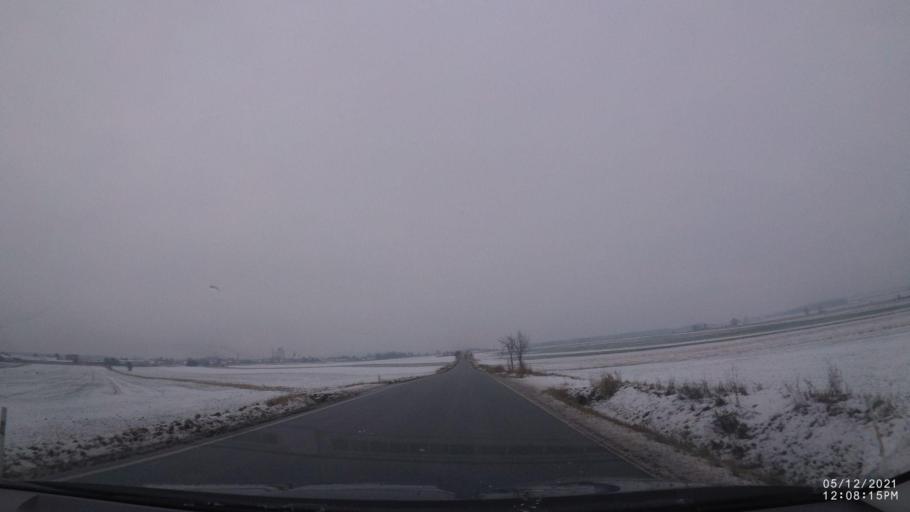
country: CZ
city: Ceske Mezirici
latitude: 50.2915
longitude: 16.0252
